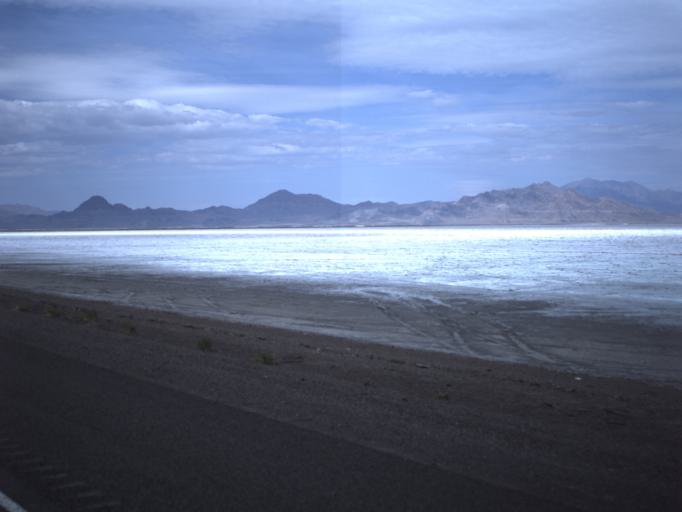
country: US
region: Utah
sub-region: Tooele County
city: Wendover
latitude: 40.7386
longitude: -113.8107
